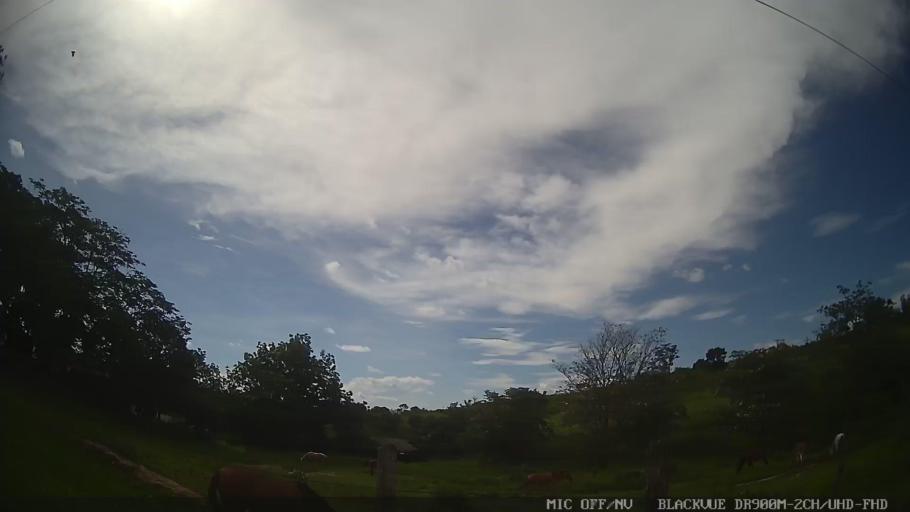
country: BR
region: Sao Paulo
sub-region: Conchas
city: Conchas
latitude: -23.0022
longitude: -48.0011
